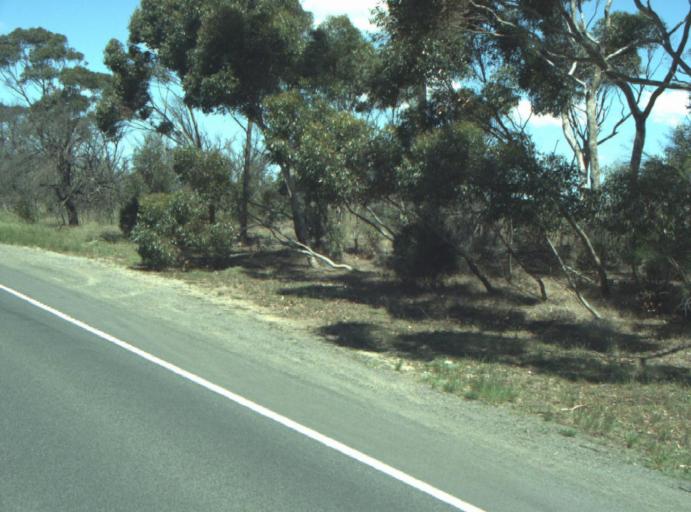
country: AU
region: Victoria
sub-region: Greater Geelong
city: Lara
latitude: -37.9579
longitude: 144.3517
